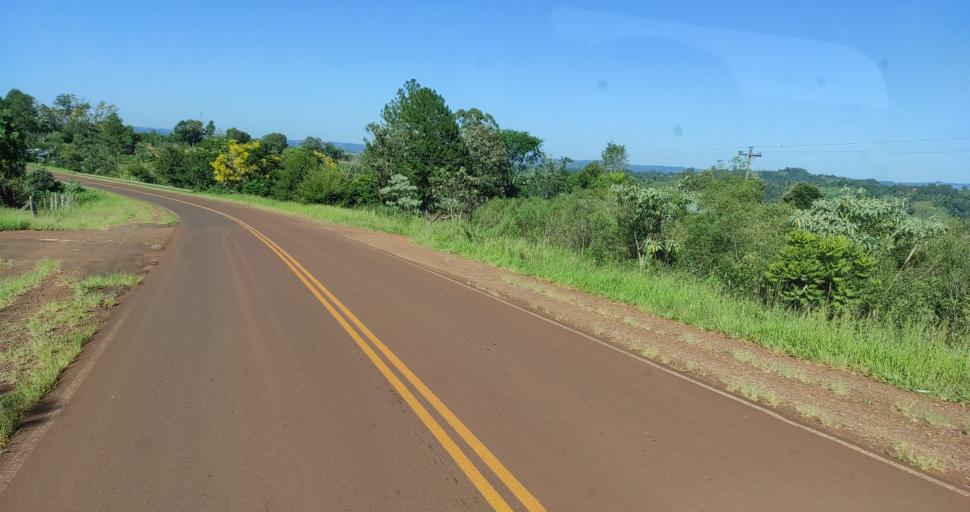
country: AR
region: Misiones
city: El Soberbio
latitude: -27.2276
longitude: -54.1770
